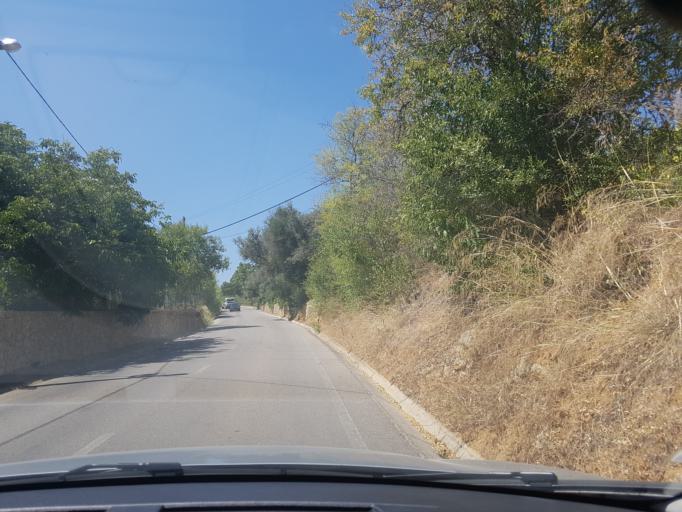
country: PT
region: Faro
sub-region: Lagoa
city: Carvoeiro
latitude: 37.1033
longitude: -8.4288
